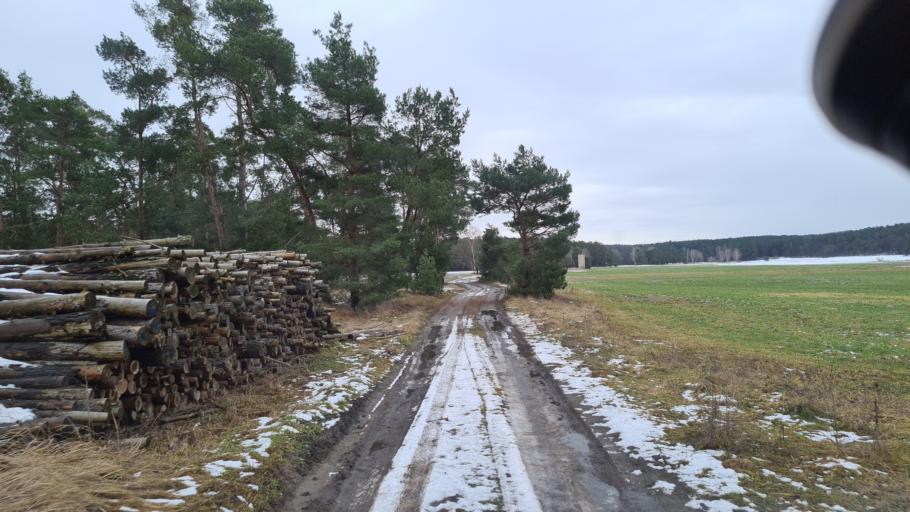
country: DE
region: Brandenburg
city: Schenkendobern
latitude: 51.9085
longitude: 14.5925
